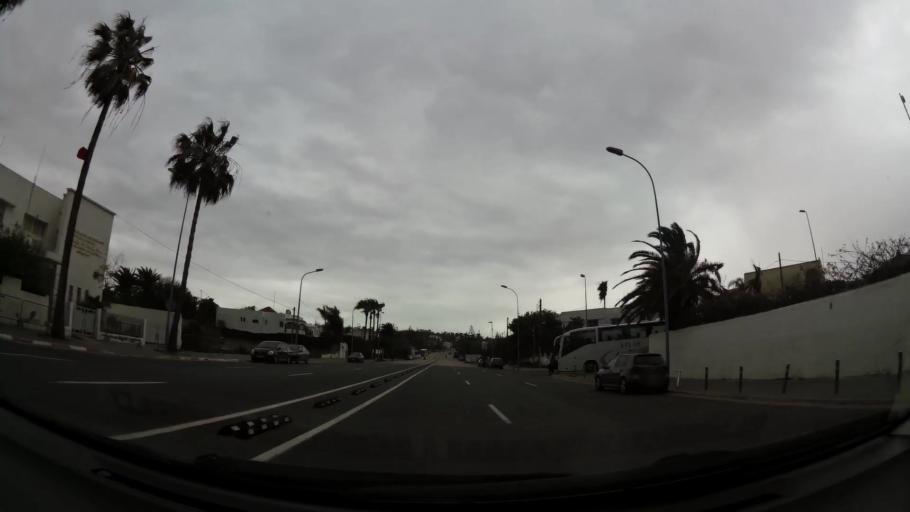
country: MA
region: Grand Casablanca
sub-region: Casablanca
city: Casablanca
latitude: 33.5913
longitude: -7.6758
